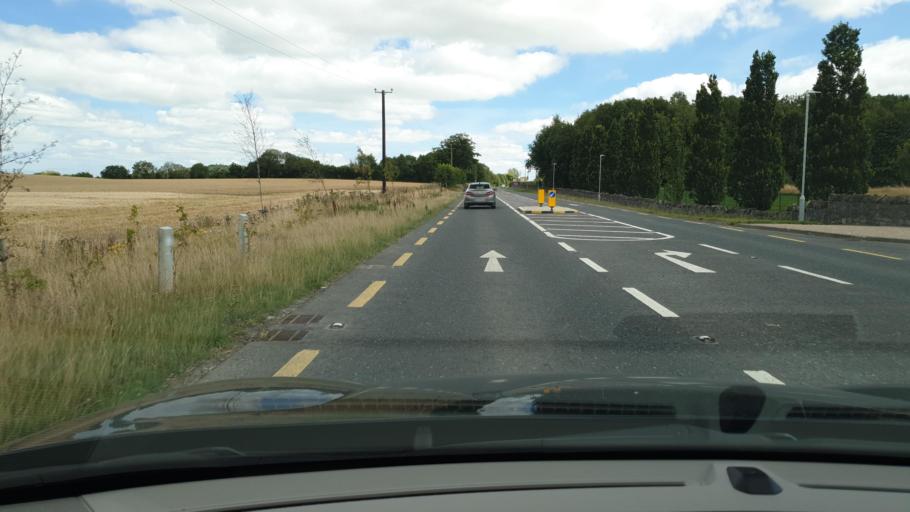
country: IE
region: Leinster
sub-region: An Mhi
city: Newtown Trim
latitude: 53.5248
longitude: -6.6662
